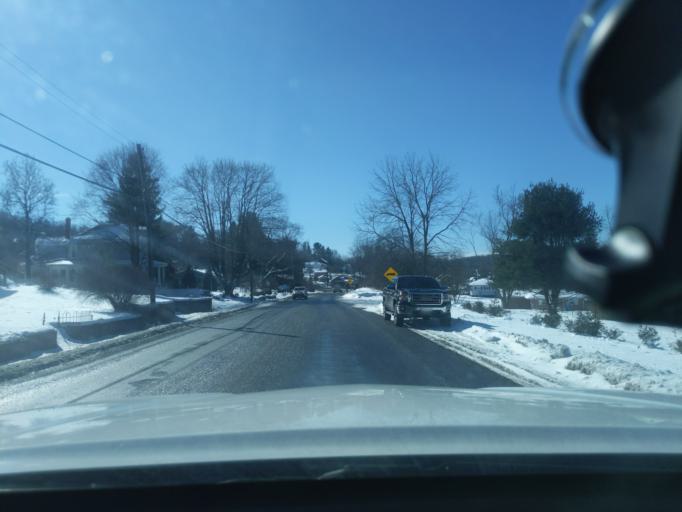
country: US
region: Maryland
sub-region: Allegany County
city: Frostburg
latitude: 39.6288
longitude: -78.9361
